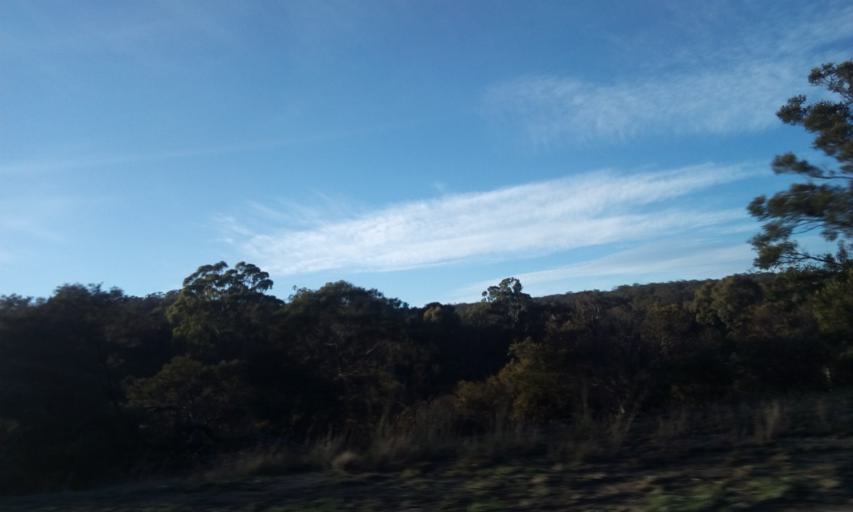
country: AU
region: New South Wales
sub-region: Yass Valley
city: Gundaroo
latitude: -35.1708
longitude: 149.3026
